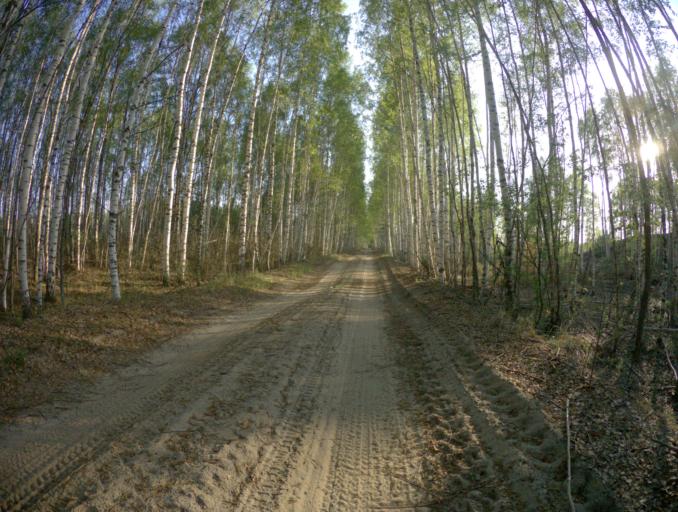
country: RU
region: Vladimir
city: Vyazniki
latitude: 56.3699
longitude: 42.1608
